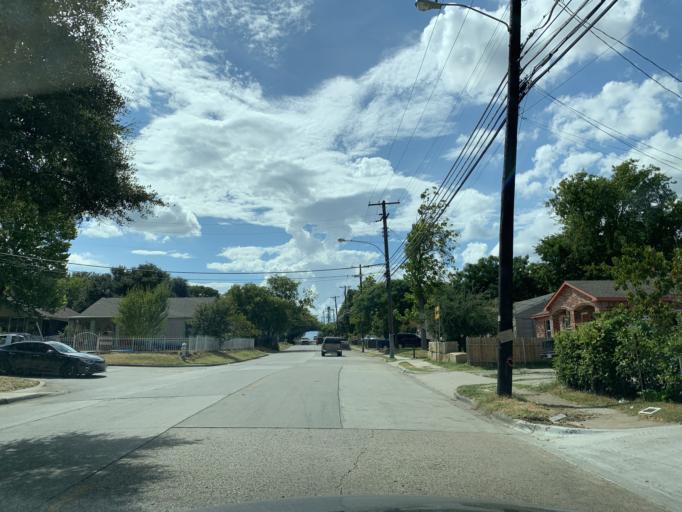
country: US
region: Texas
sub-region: Dallas County
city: Cockrell Hill
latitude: 32.7350
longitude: -96.8778
